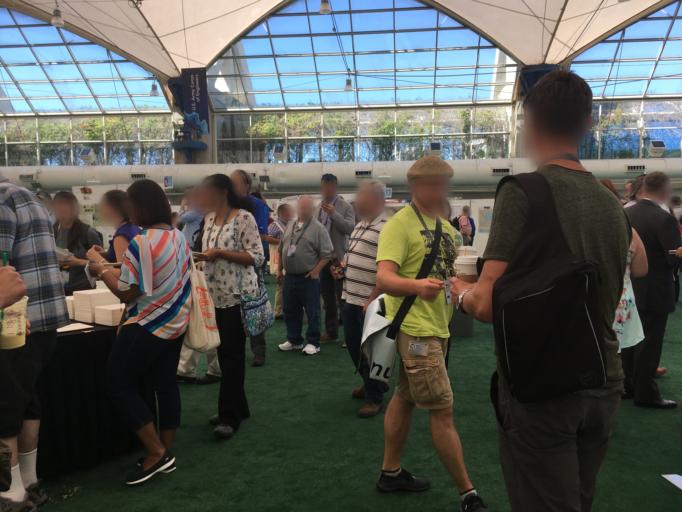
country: US
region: California
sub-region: San Diego County
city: San Diego
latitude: 32.7069
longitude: -117.1620
